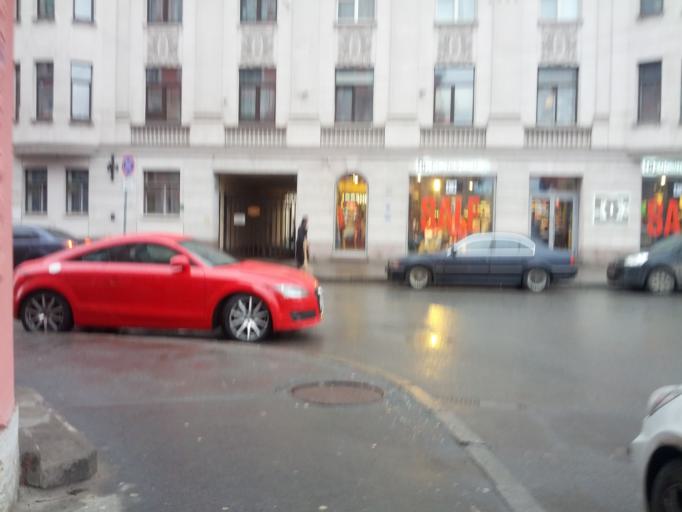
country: RU
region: St.-Petersburg
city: Petrogradka
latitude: 59.9603
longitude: 30.3117
